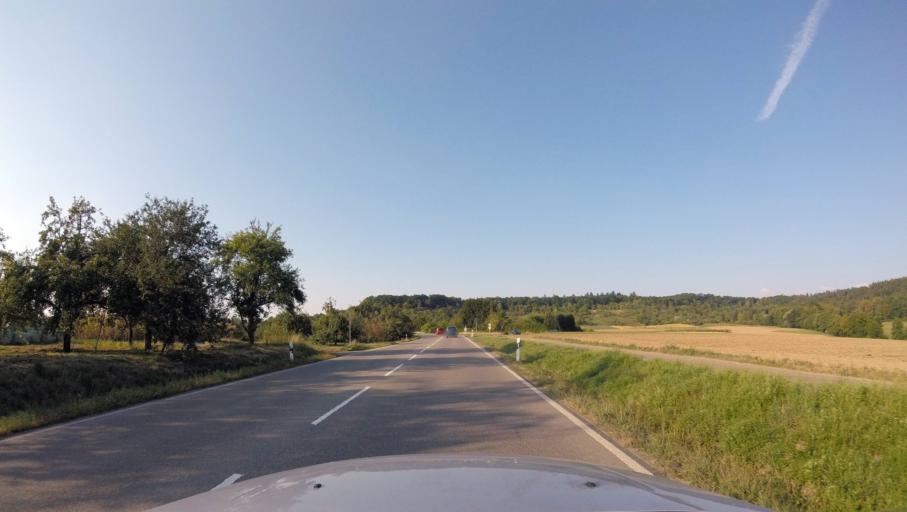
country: DE
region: Baden-Wuerttemberg
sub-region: Regierungsbezirk Stuttgart
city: Leutenbach
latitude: 48.8950
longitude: 9.4241
